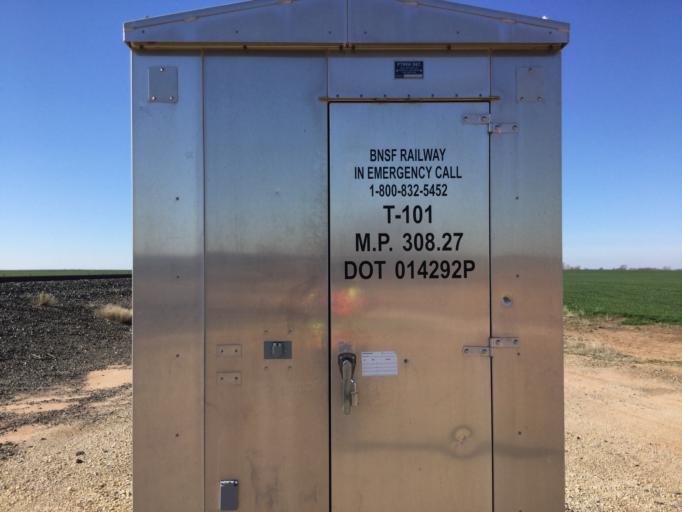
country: US
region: Kansas
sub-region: Barber County
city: Kiowa
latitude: 36.9986
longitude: -98.5039
